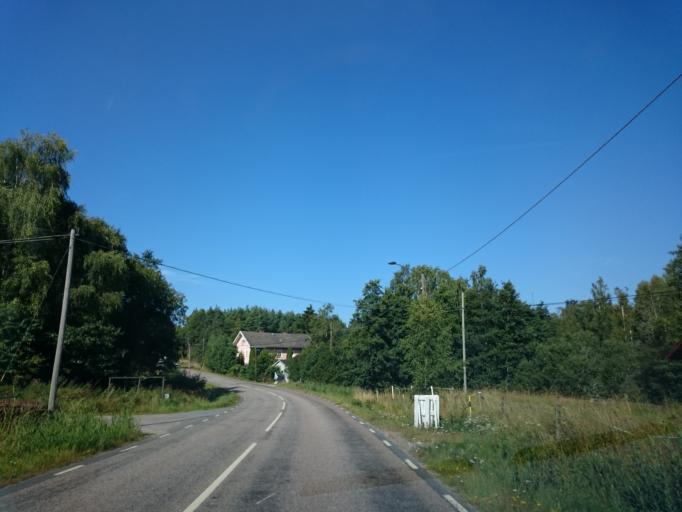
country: SE
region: OEstergoetland
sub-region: Norrkopings Kommun
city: Krokek
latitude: 58.6591
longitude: 16.4956
